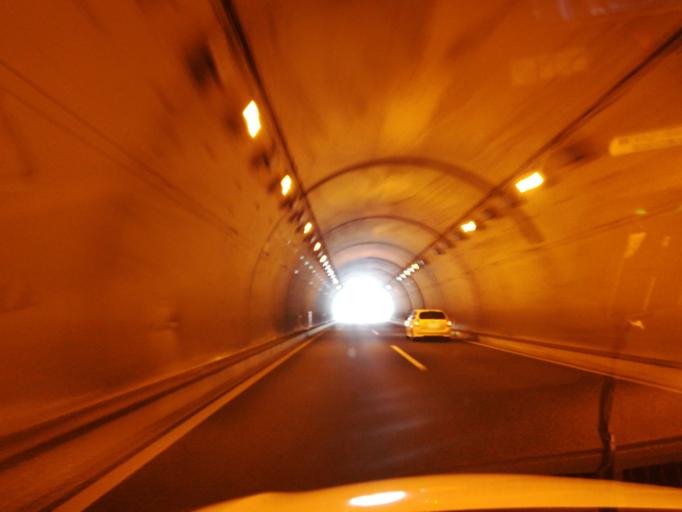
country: JP
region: Kochi
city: Kochi-shi
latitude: 33.7751
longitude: 133.6606
